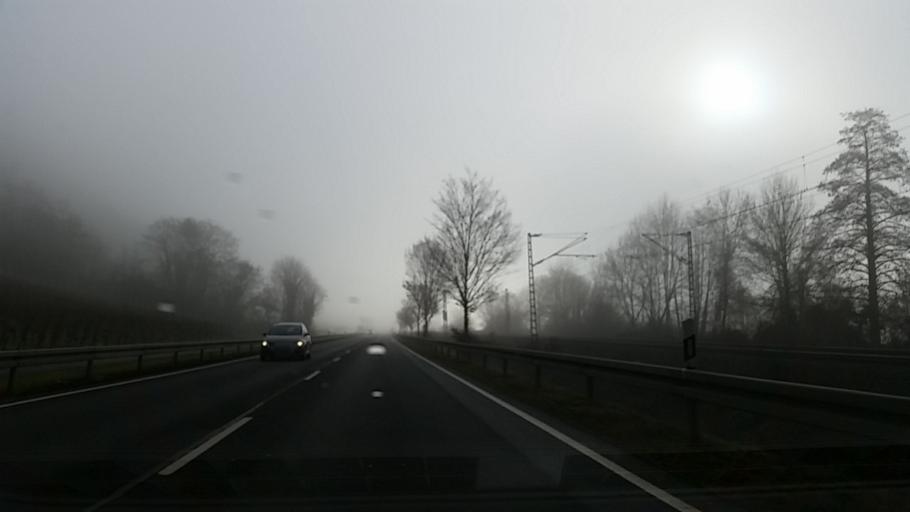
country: DE
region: Bavaria
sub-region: Regierungsbezirk Unterfranken
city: Erlabrunn
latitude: 49.8544
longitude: 9.8597
